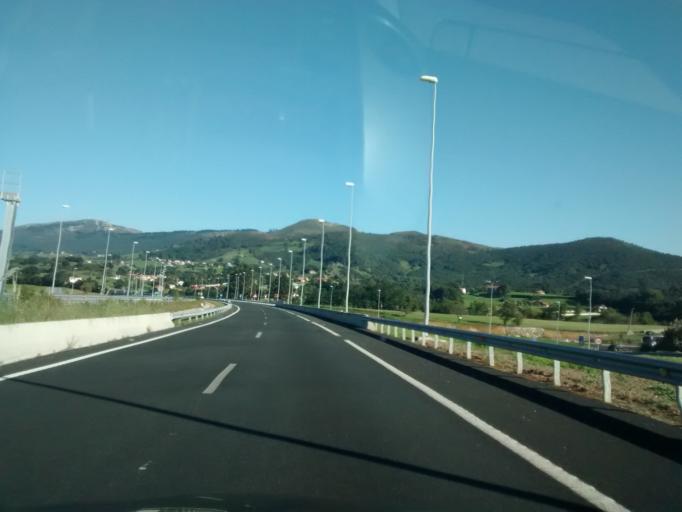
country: ES
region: Cantabria
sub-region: Provincia de Cantabria
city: Camargo
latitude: 43.3851
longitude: -3.8594
